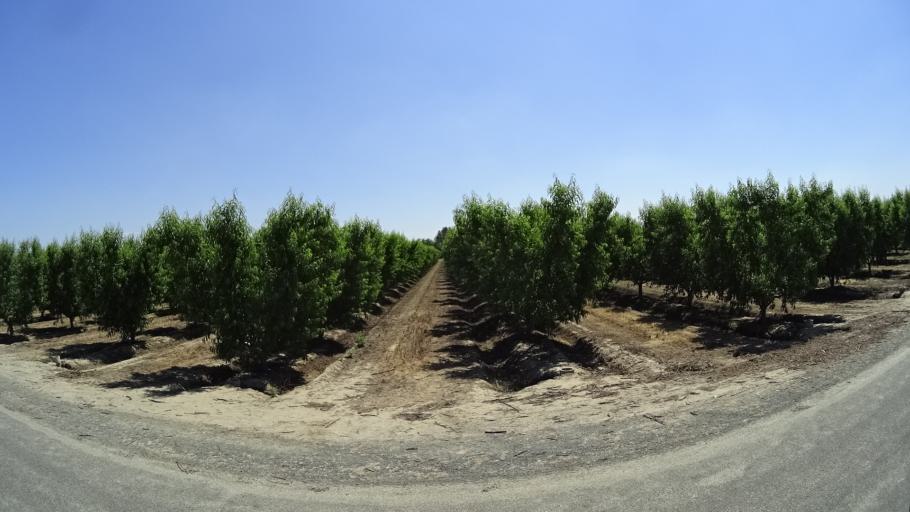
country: US
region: California
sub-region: Fresno County
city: Kingsburg
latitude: 36.4655
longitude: -119.5823
